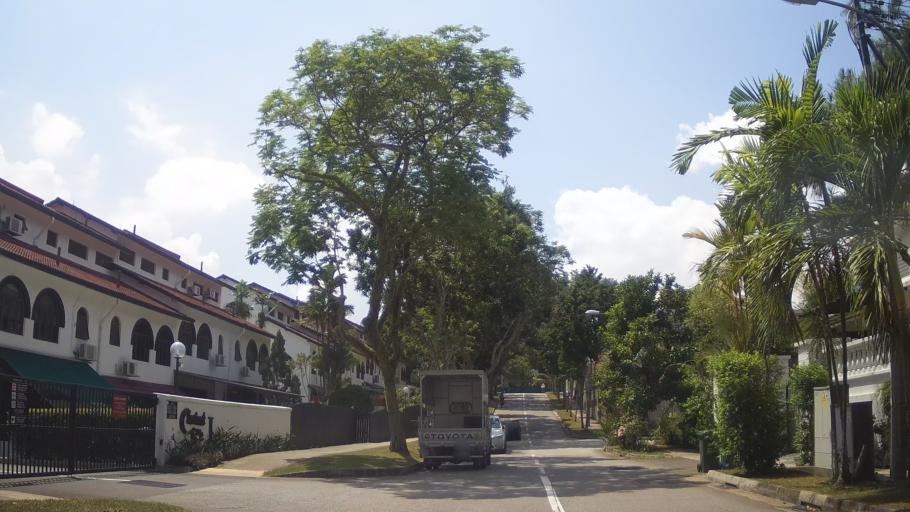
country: MY
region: Johor
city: Johor Bahru
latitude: 1.3676
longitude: 103.7700
